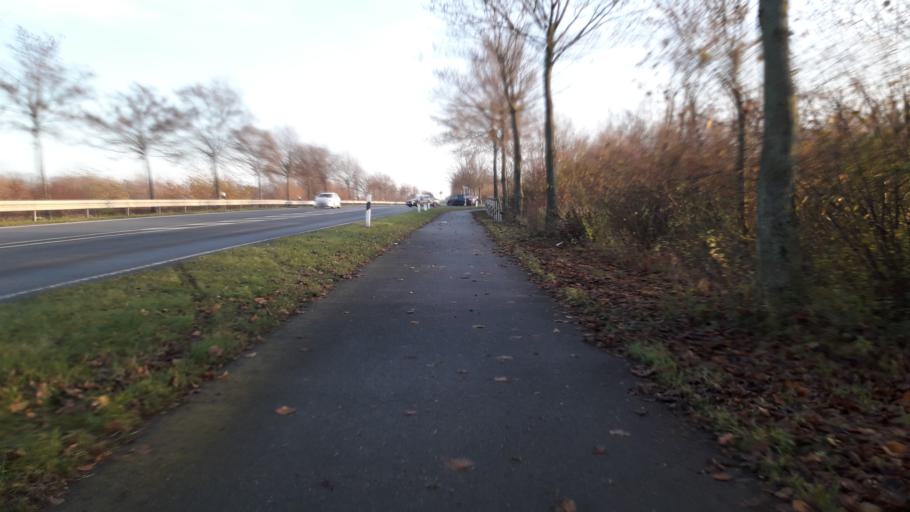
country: DE
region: North Rhine-Westphalia
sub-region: Regierungsbezirk Detmold
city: Paderborn
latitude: 51.7275
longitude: 8.7994
